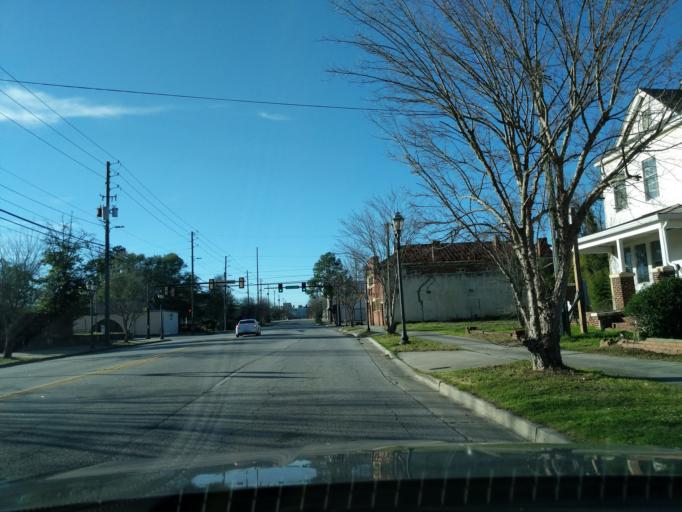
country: US
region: Georgia
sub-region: Richmond County
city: Augusta
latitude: 33.4646
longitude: -81.9763
